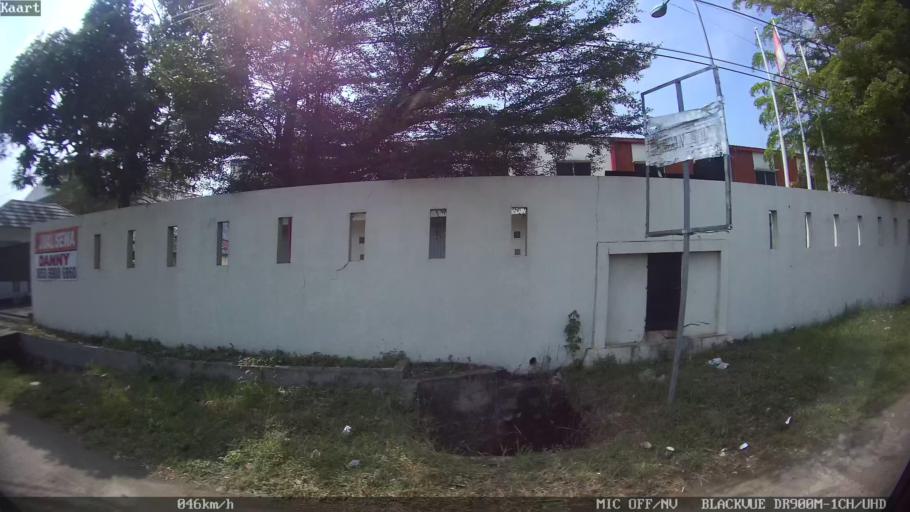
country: ID
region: Lampung
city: Gadingrejo
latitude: -5.3818
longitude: 105.0222
